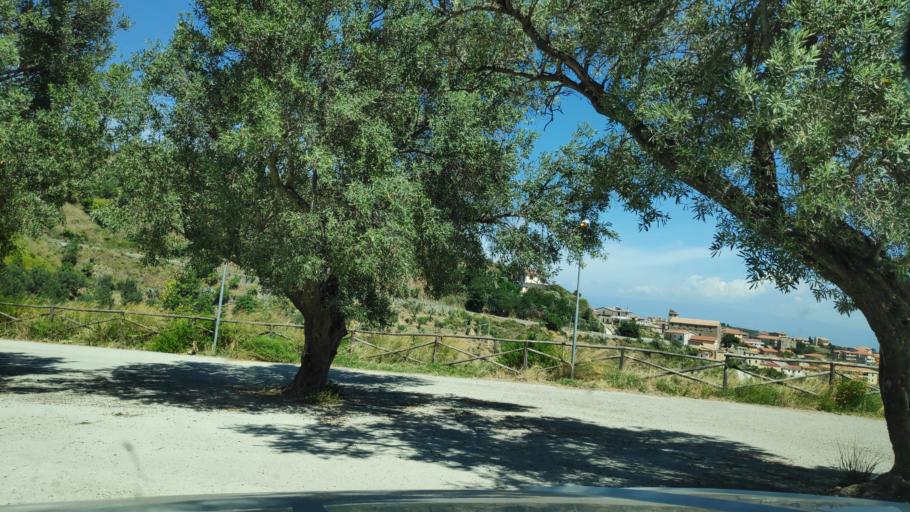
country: IT
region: Calabria
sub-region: Provincia di Catanzaro
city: Montauro
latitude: 38.7441
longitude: 16.5109
